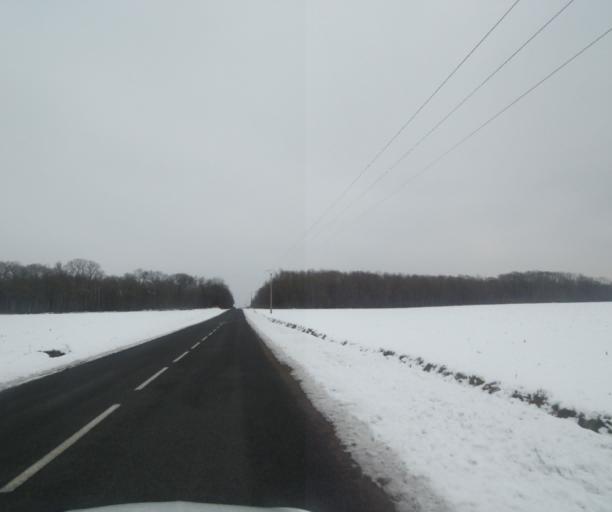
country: FR
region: Champagne-Ardenne
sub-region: Departement de la Haute-Marne
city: Villiers-en-Lieu
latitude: 48.6075
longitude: 4.8826
